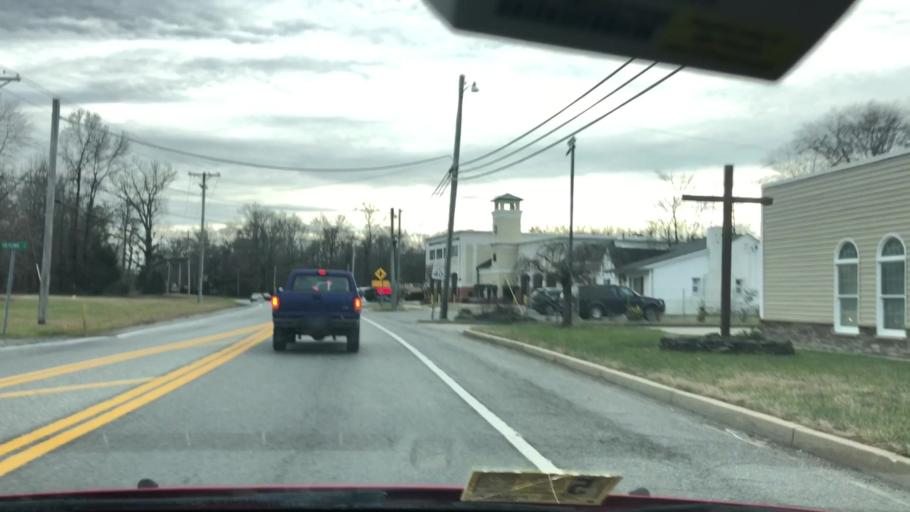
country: US
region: Maryland
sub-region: Charles County
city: Bryans Road
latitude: 38.6254
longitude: -77.0736
